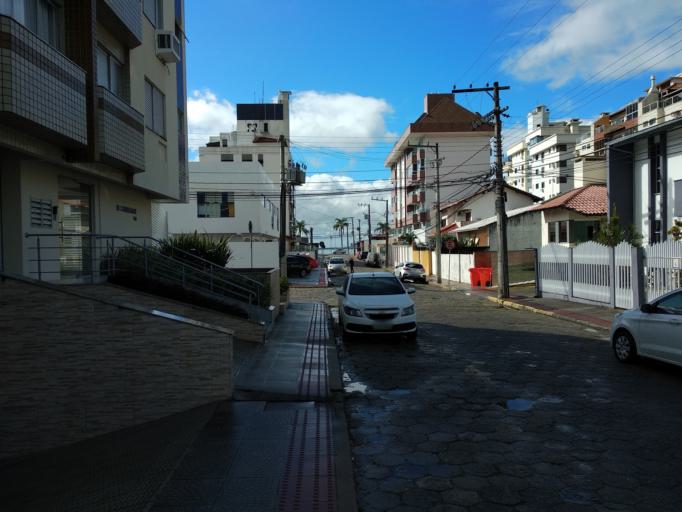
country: BR
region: Santa Catarina
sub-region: Sao Jose
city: Campinas
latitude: -27.6118
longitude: -48.5852
